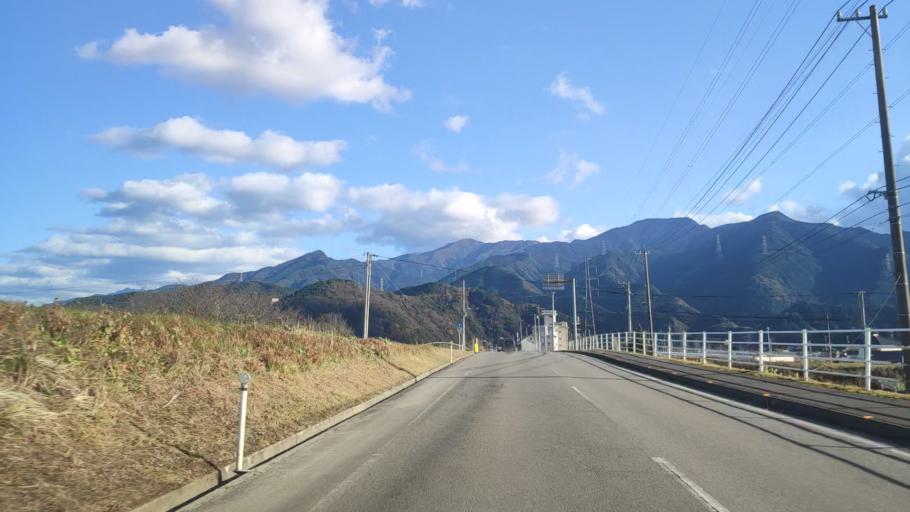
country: JP
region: Ehime
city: Saijo
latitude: 33.9039
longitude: 133.1807
